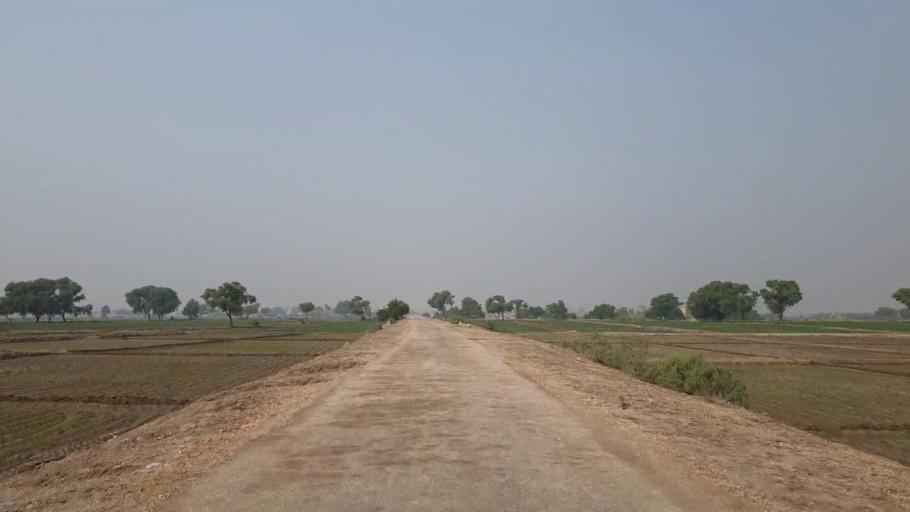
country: PK
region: Sindh
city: Bhan
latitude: 26.4978
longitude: 67.6972
